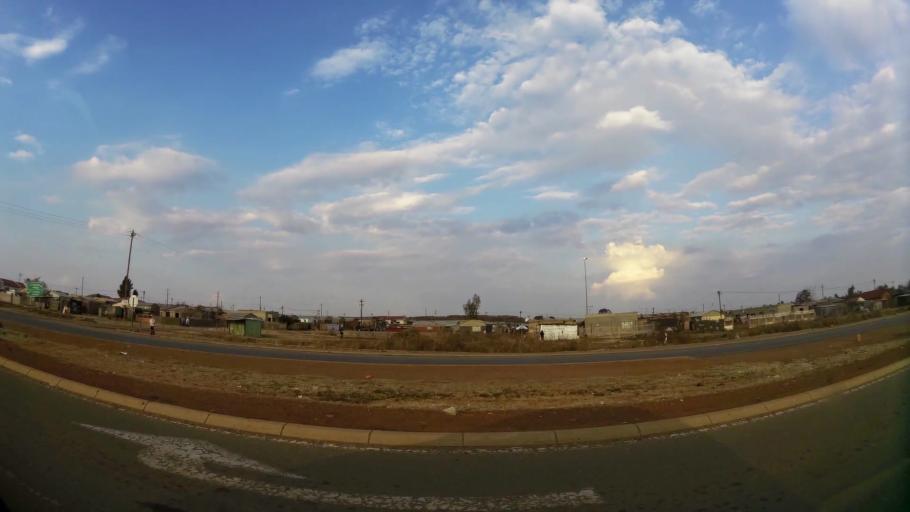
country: ZA
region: Gauteng
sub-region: Sedibeng District Municipality
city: Vanderbijlpark
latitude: -26.6023
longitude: 27.8180
